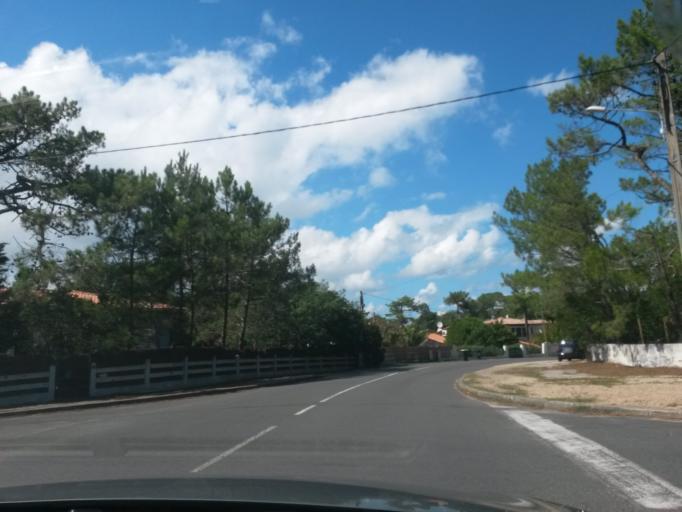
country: FR
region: Aquitaine
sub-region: Departement de la Gironde
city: Arcachon
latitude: 44.6511
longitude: -1.2493
